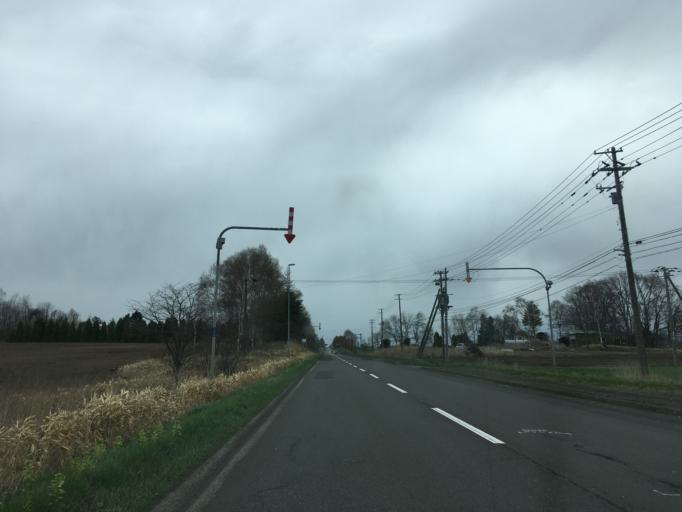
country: JP
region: Hokkaido
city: Chitose
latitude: 42.9113
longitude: 141.8112
